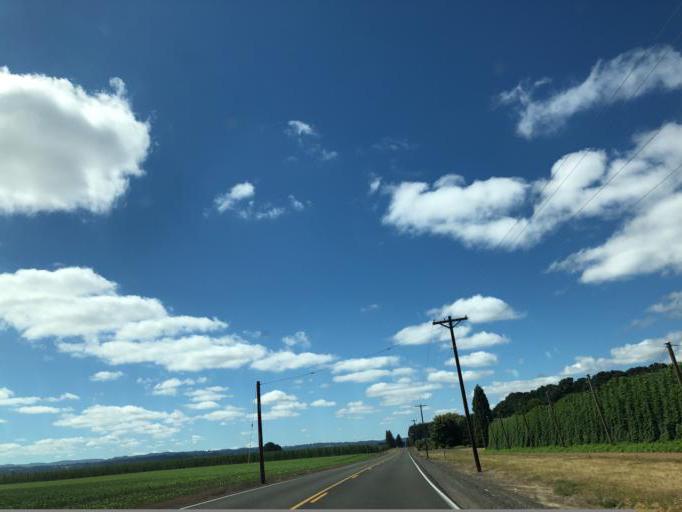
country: US
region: Oregon
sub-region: Marion County
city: Mount Angel
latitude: 45.0936
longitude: -122.7435
